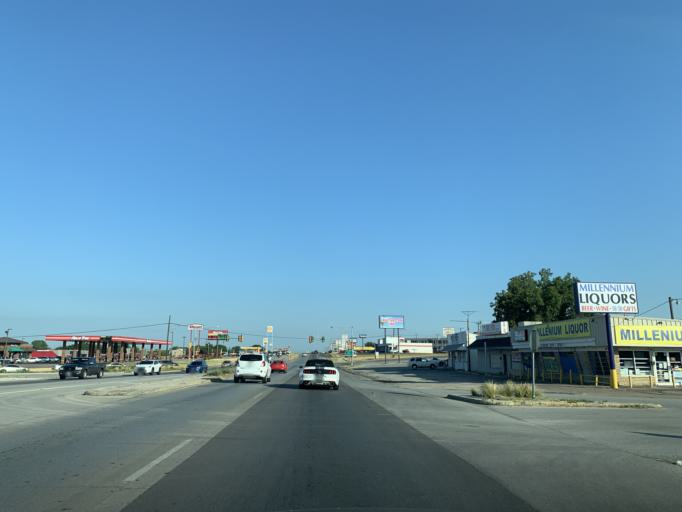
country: US
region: Texas
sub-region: Tarrant County
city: Sansom Park
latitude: 32.8033
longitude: -97.4109
